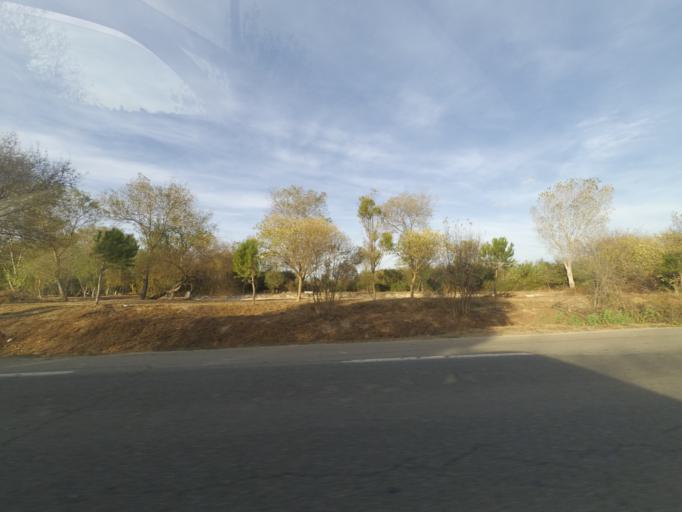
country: FR
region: Languedoc-Roussillon
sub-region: Departement du Gard
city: Aimargues
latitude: 43.6873
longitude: 4.2226
